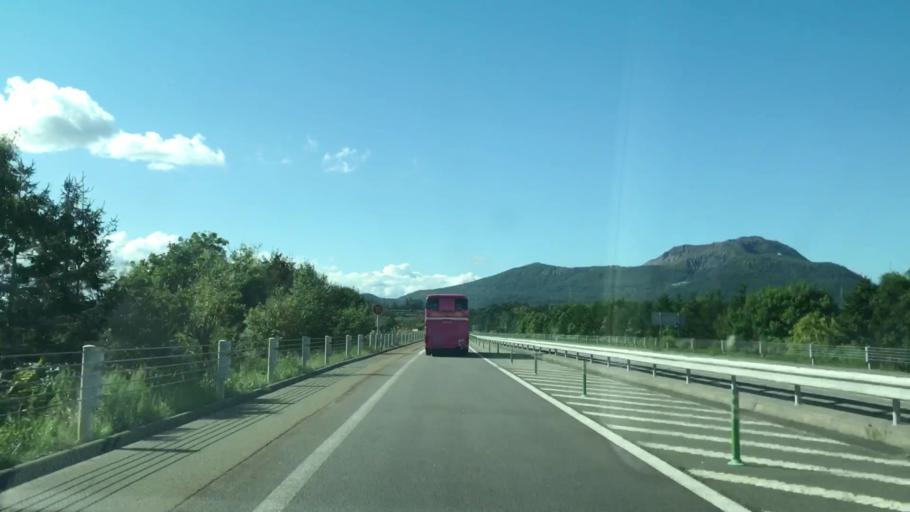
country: JP
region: Hokkaido
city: Date
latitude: 42.4913
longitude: 140.8786
